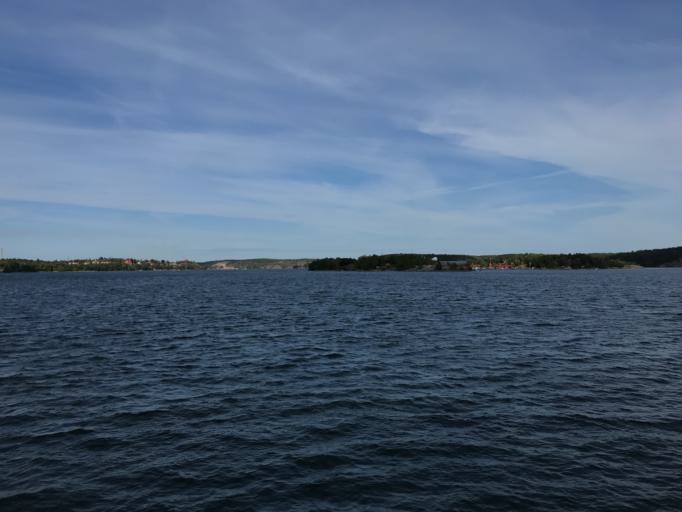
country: SE
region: Stockholm
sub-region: Nacka Kommun
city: Nacka
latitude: 59.3313
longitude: 18.1561
